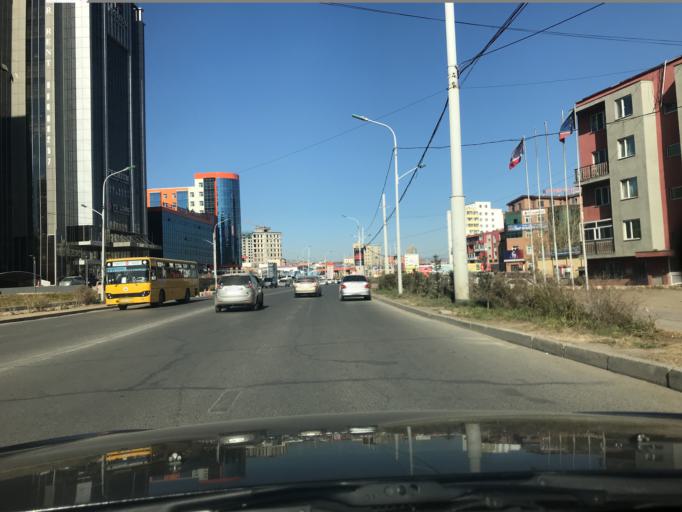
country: MN
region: Ulaanbaatar
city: Ulaanbaatar
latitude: 47.9237
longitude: 106.9013
